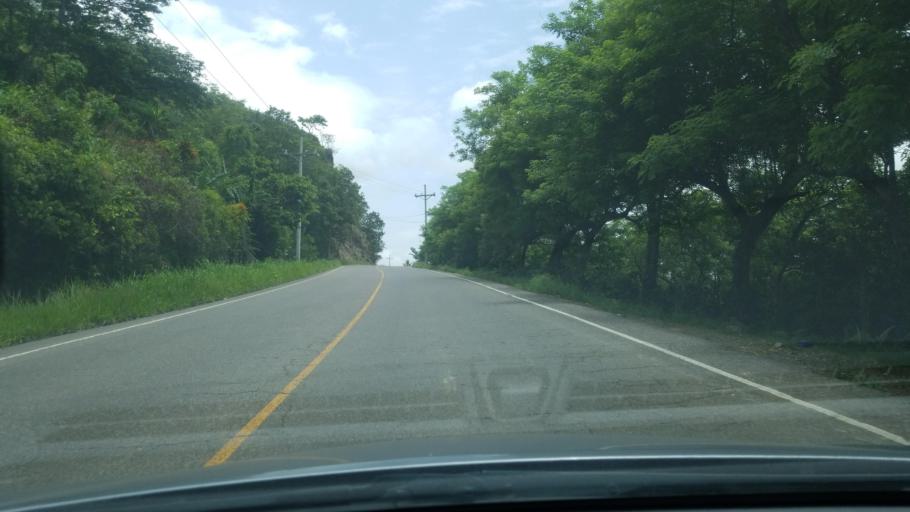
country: HN
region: Copan
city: Cucuyagua
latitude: 14.6692
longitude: -88.8434
